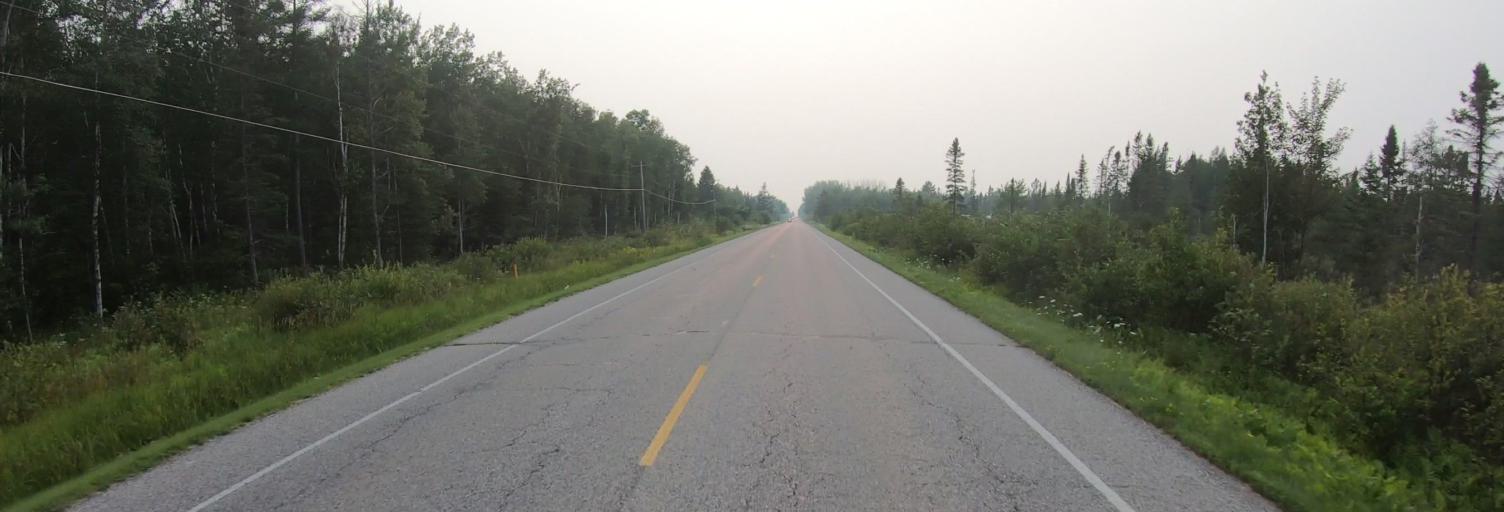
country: US
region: Michigan
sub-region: Chippewa County
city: Sault Ste. Marie
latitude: 46.4188
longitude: -84.4917
